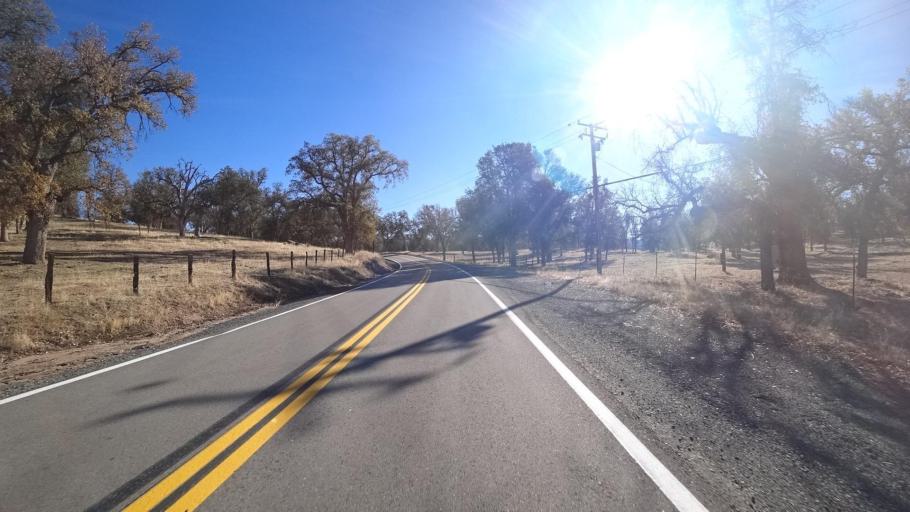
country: US
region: California
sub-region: Kern County
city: Alta Sierra
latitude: 35.7116
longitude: -118.7374
